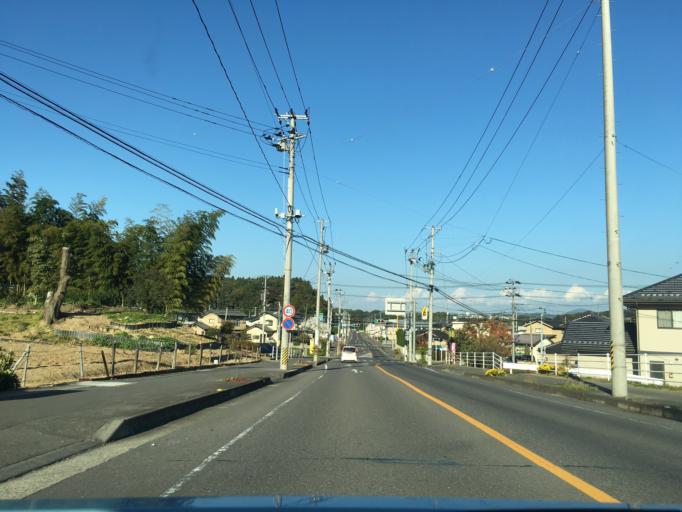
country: JP
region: Fukushima
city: Sukagawa
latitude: 37.3068
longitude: 140.3729
